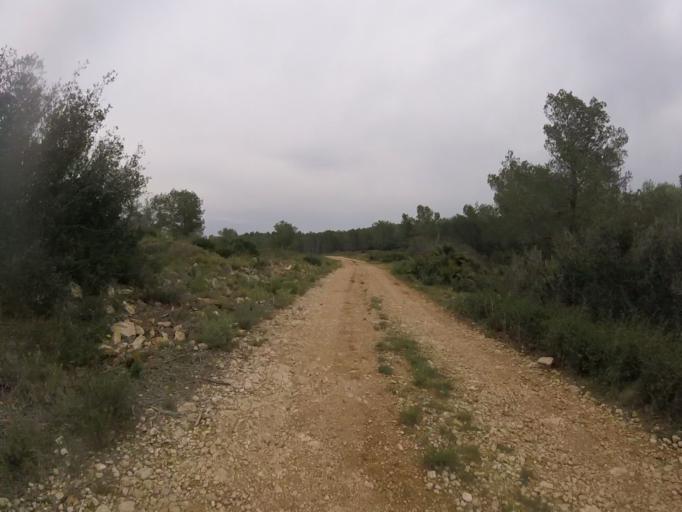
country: ES
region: Valencia
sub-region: Provincia de Castello
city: Alcala de Xivert
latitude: 40.3156
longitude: 0.2686
